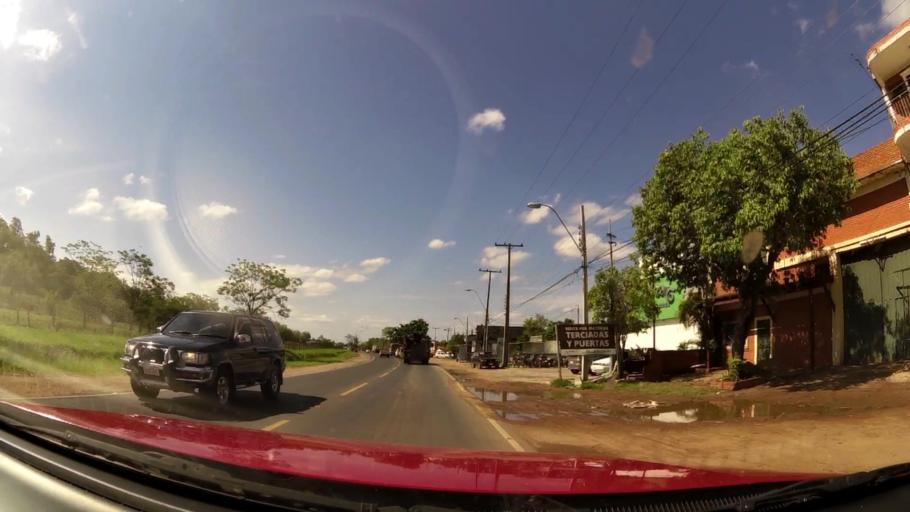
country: PY
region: Central
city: Fernando de la Mora
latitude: -25.2767
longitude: -57.5232
